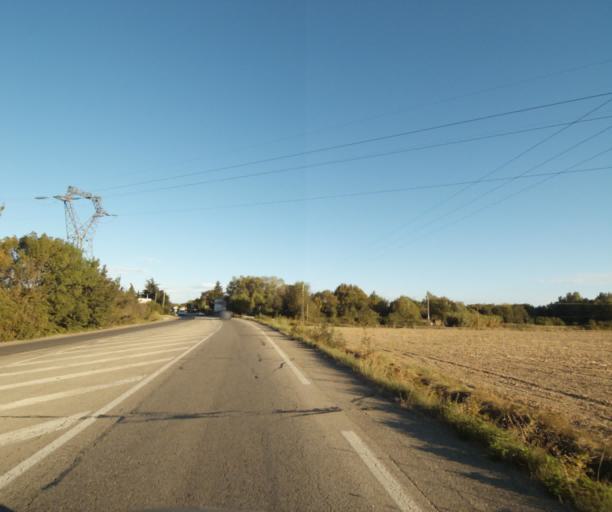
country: FR
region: Languedoc-Roussillon
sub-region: Departement du Gard
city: Caissargues
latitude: 43.8127
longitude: 4.3992
